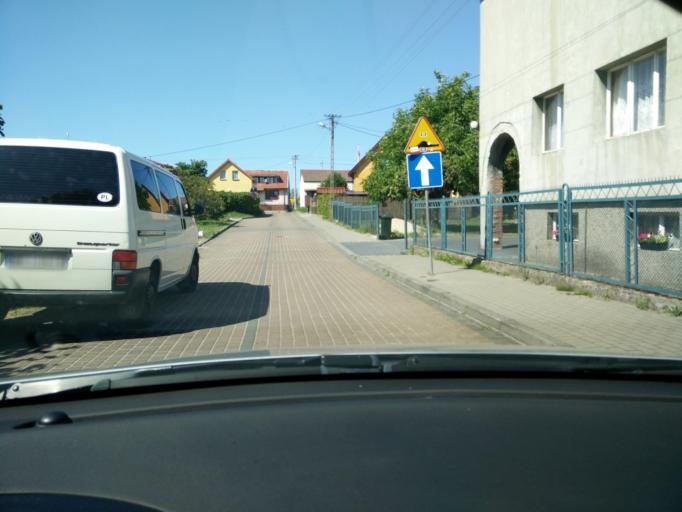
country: PL
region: Pomeranian Voivodeship
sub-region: Powiat pucki
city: Mosty
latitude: 54.6313
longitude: 18.5009
